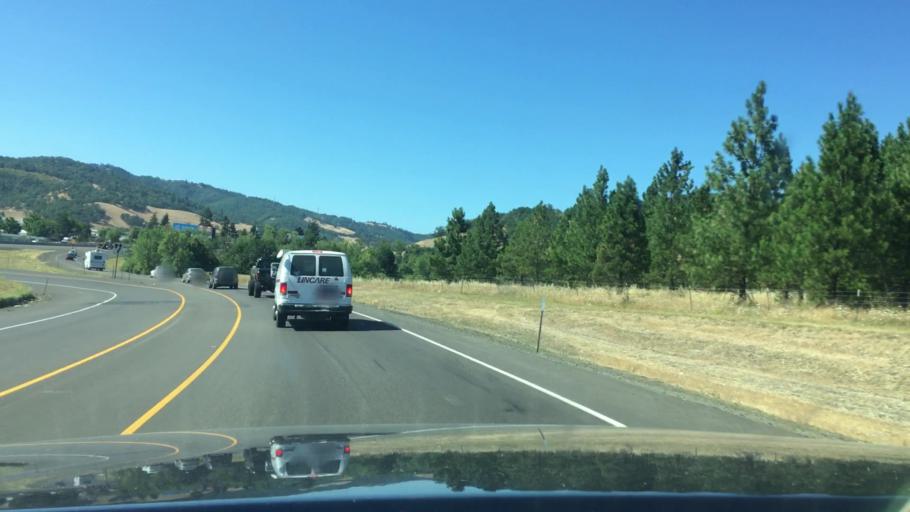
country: US
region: Oregon
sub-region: Douglas County
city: Green
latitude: 43.1560
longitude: -123.3631
